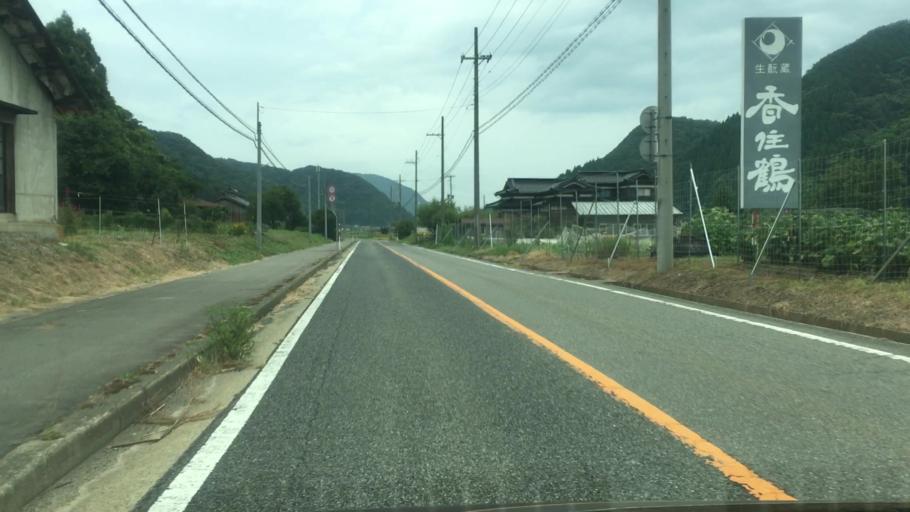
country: JP
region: Hyogo
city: Toyooka
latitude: 35.6307
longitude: 134.6799
